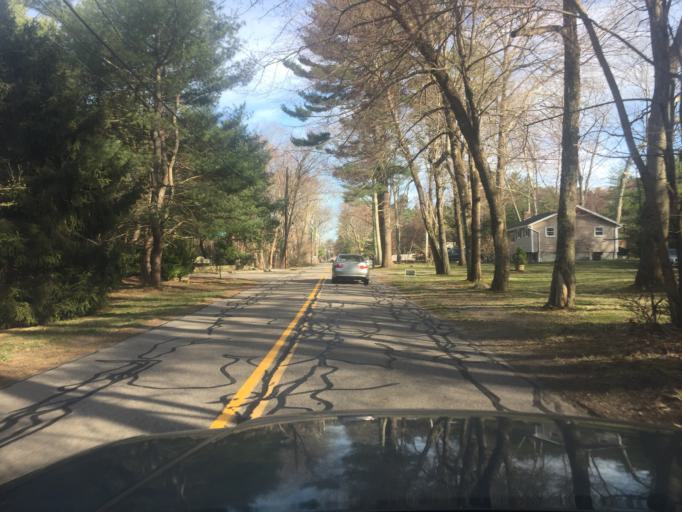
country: US
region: Massachusetts
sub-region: Norfolk County
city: Medway
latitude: 42.1288
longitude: -71.4424
